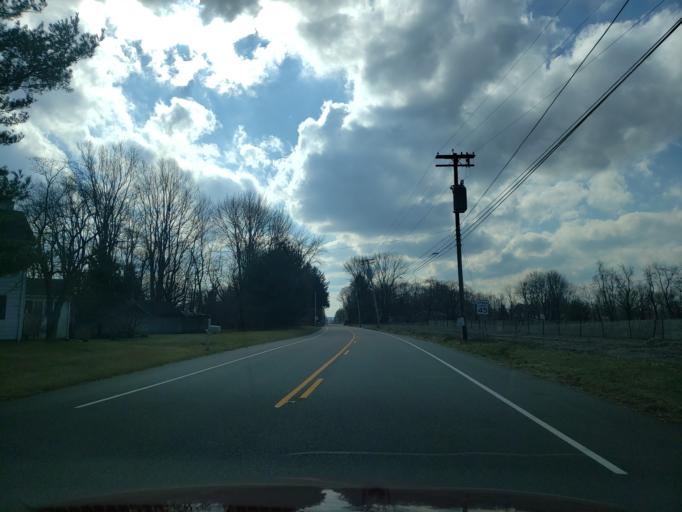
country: US
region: New Jersey
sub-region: Hunterdon County
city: Lambertville
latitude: 40.4525
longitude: -74.9375
